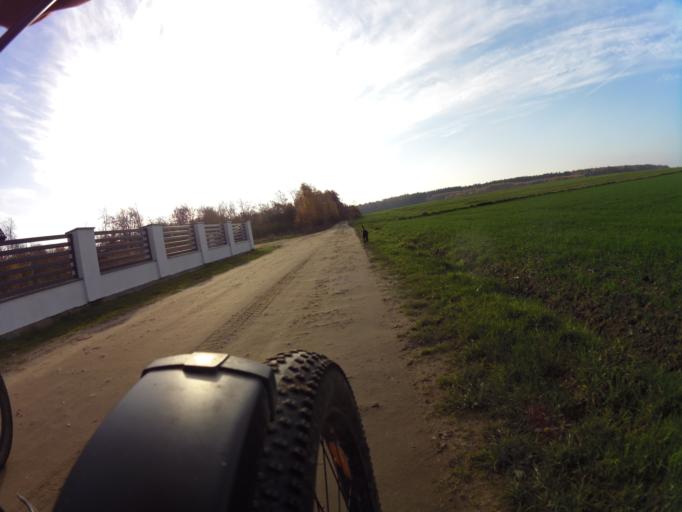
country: PL
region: Pomeranian Voivodeship
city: Strzelno
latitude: 54.7481
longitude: 18.2883
